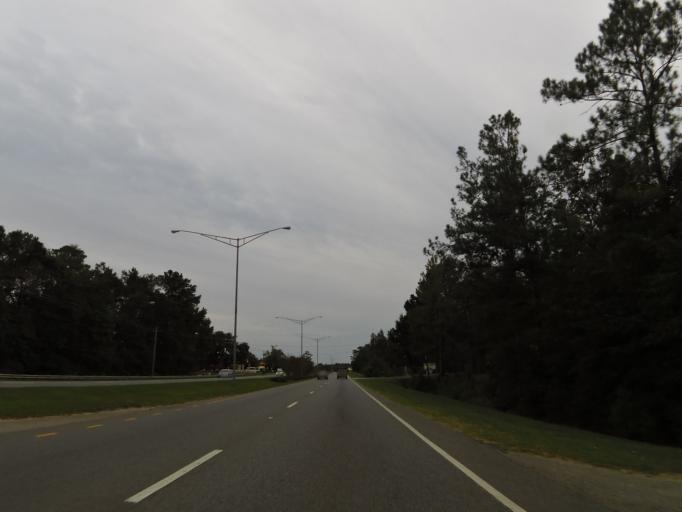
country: US
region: Alabama
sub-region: Baldwin County
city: Bay Minette
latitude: 30.8584
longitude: -87.7768
